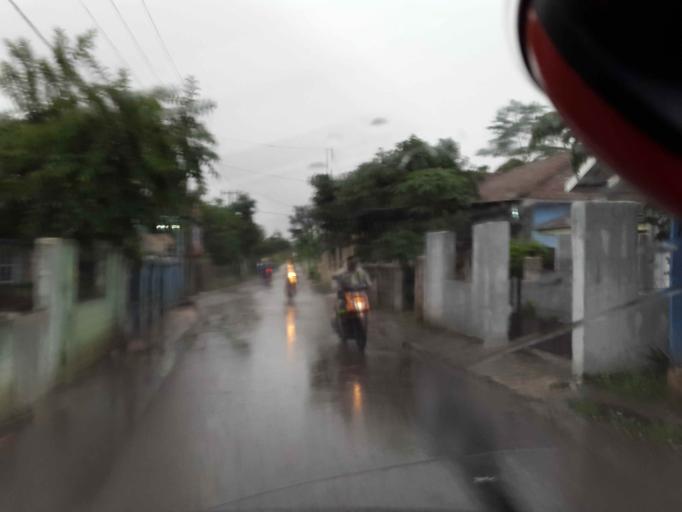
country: ID
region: West Java
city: Padalarang
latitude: -6.9049
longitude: 107.4586
